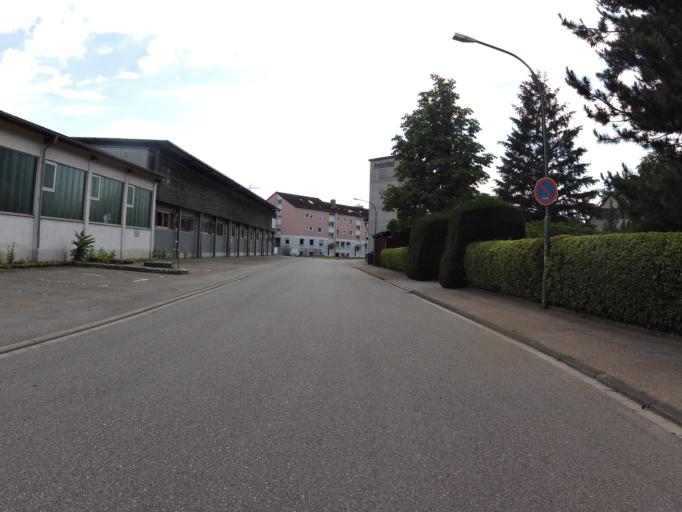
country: DE
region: Baden-Wuerttemberg
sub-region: Freiburg Region
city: Lahr
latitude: 48.3365
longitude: 7.8551
